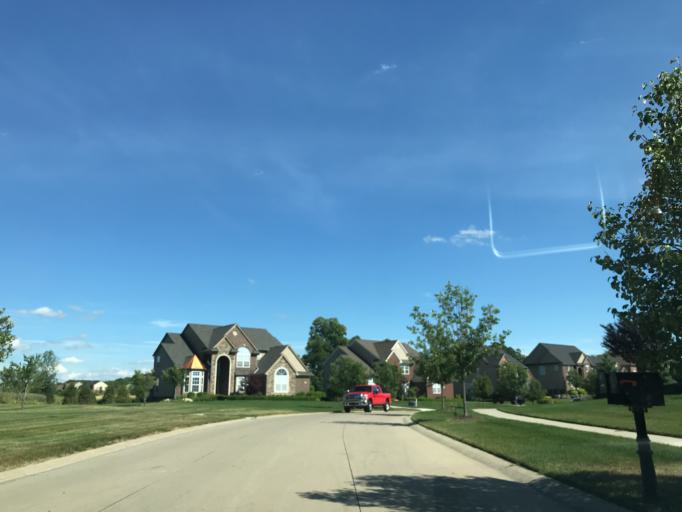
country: US
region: Michigan
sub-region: Oakland County
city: Wixom
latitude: 42.4624
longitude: -83.5671
